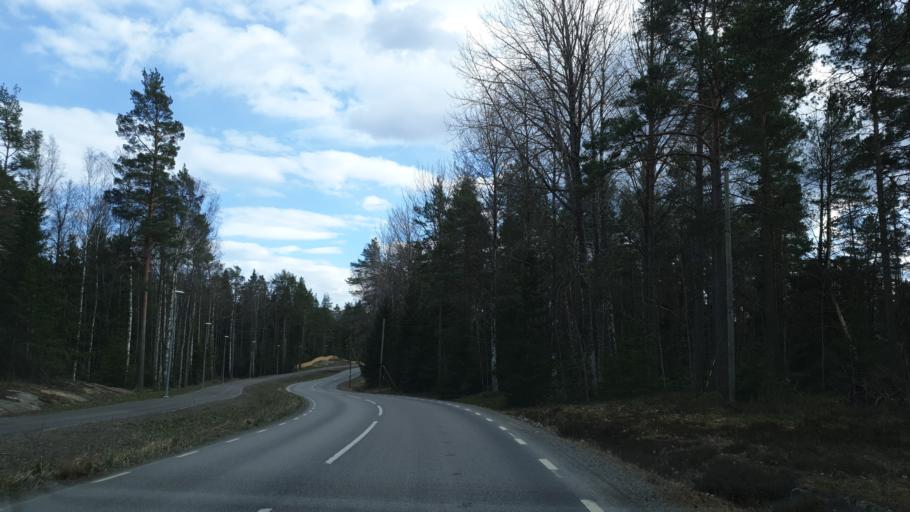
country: SE
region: Stockholm
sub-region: Varmdo Kommun
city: Mortnas
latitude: 59.2703
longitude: 18.4261
